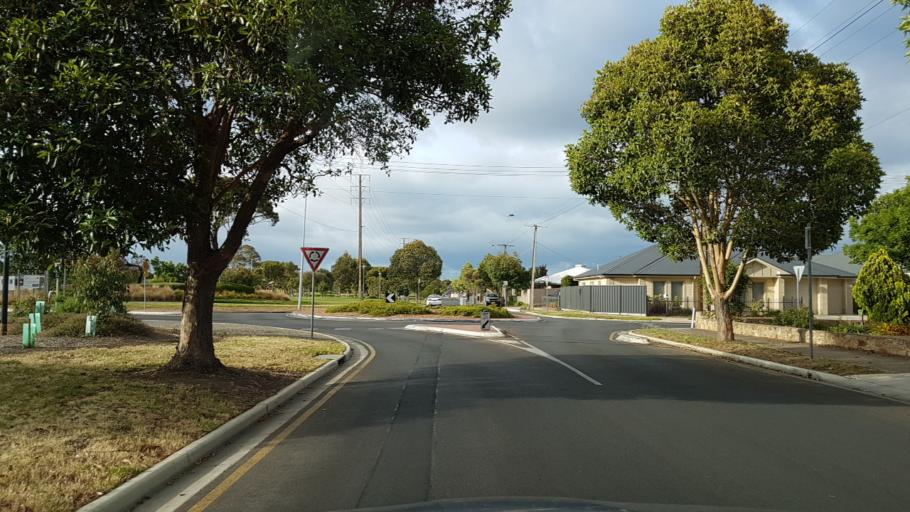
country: AU
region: South Australia
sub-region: City of West Torrens
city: Plympton
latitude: -34.9540
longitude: 138.5590
